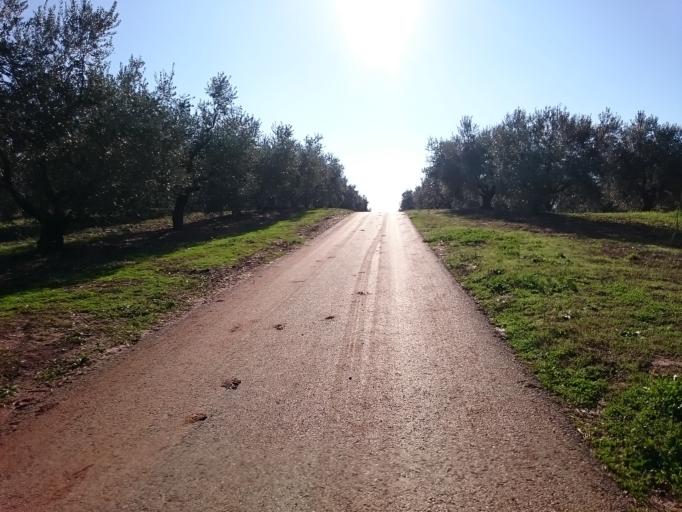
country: HR
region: Istarska
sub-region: Grad Porec
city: Porec
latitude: 45.2621
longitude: 13.5847
